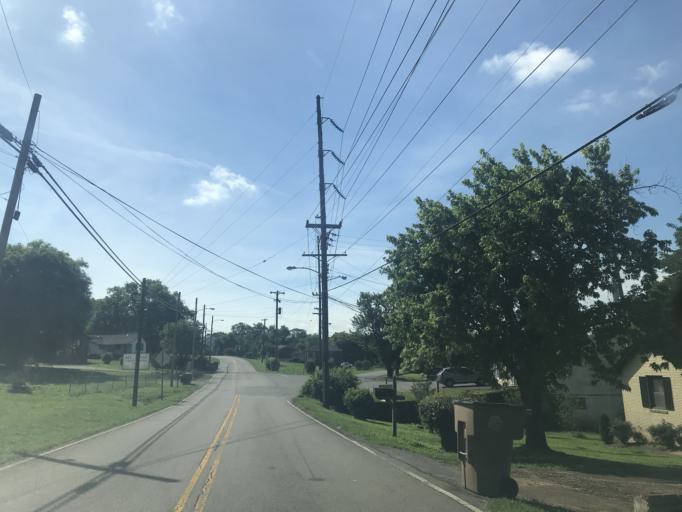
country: US
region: Tennessee
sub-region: Davidson County
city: Nashville
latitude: 36.1971
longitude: -86.8434
